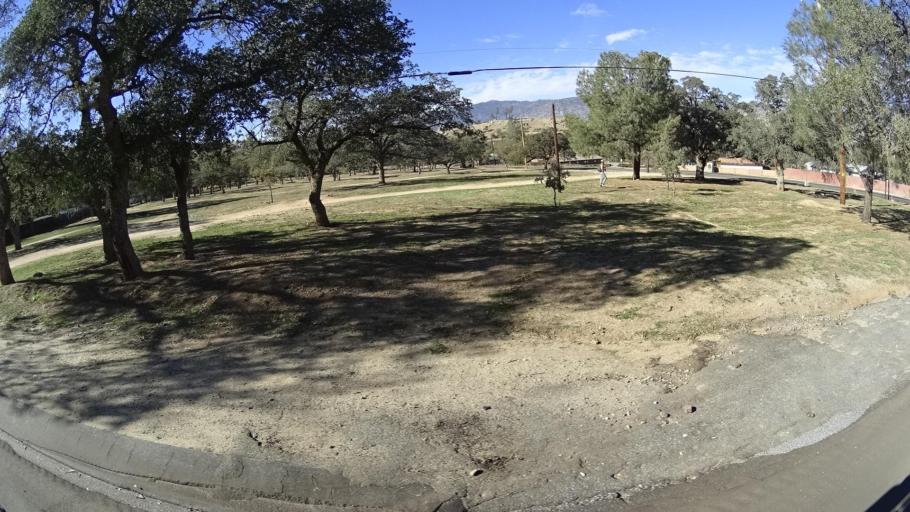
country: US
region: California
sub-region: Kern County
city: Bodfish
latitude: 35.5896
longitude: -118.4955
